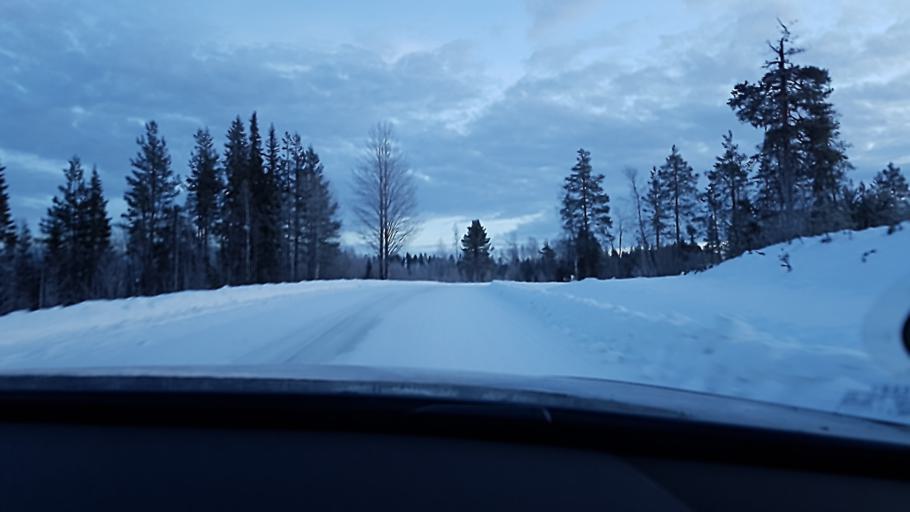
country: SE
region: Vaesterbotten
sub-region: Sorsele Kommun
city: Sorsele
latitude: 65.5023
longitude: 17.5511
